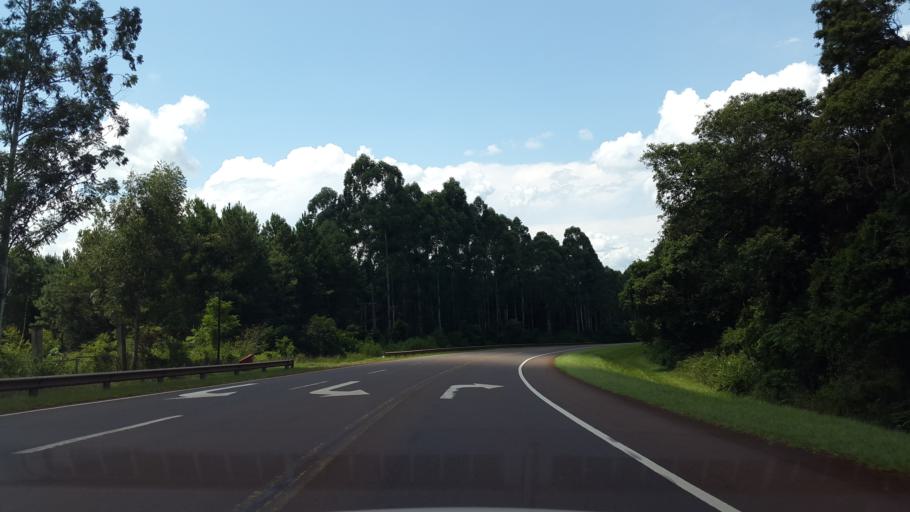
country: AR
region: Misiones
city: El Alcazar
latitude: -26.6935
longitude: -54.8315
